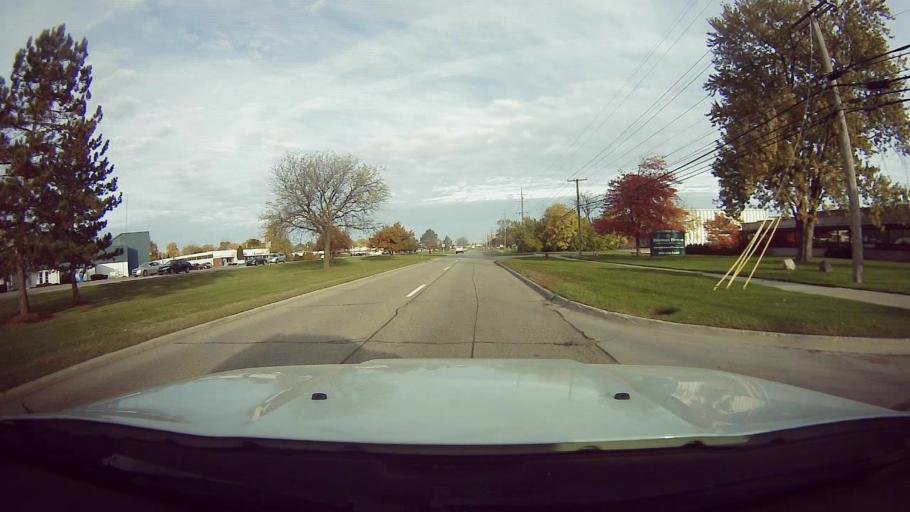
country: US
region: Michigan
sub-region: Oakland County
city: Clawson
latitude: 42.5511
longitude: -83.1233
